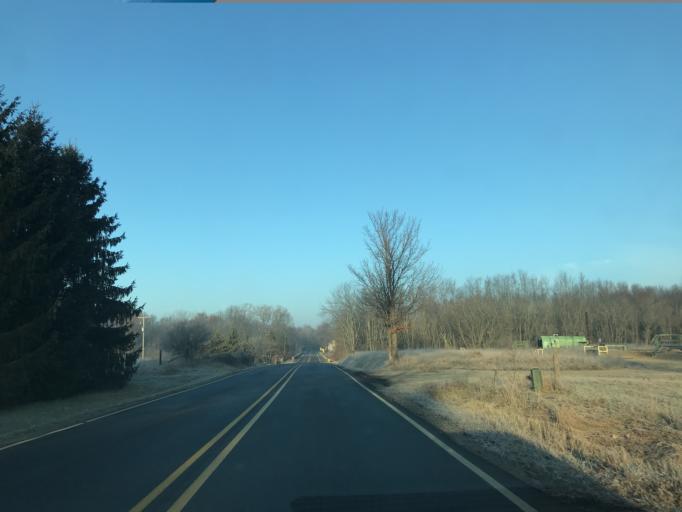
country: US
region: Michigan
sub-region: Eaton County
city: Eaton Rapids
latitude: 42.4408
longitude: -84.5547
